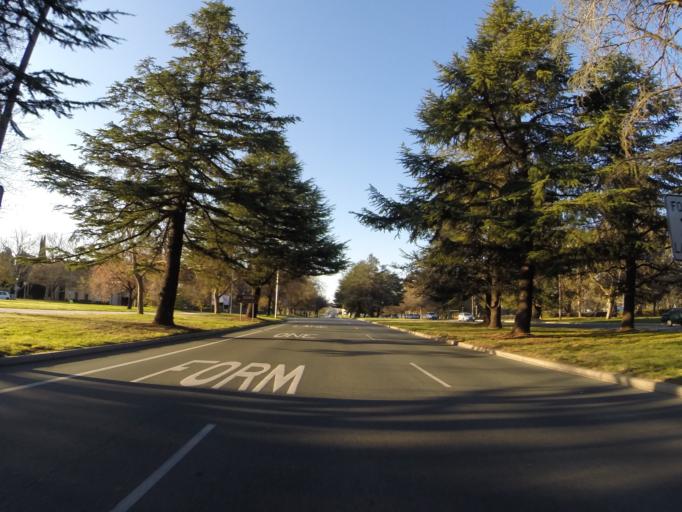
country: AU
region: Australian Capital Territory
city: Canberra
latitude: -35.2990
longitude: 149.1258
